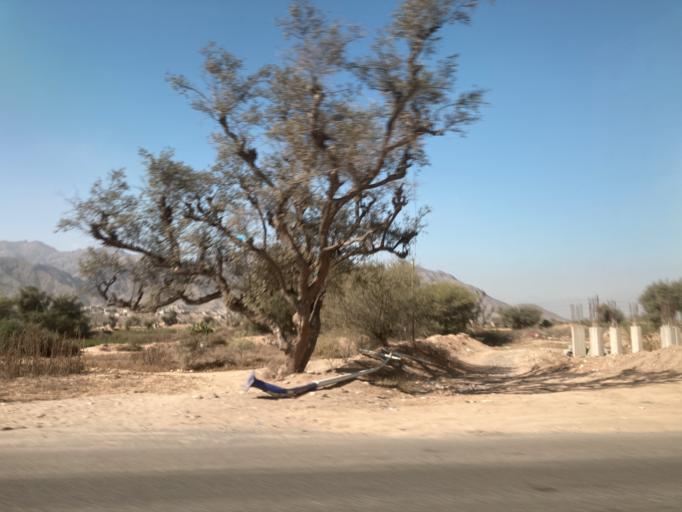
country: YE
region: Ad Dali'
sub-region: Qa'atabah
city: Qa`tabah
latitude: 13.8116
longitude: 44.7216
